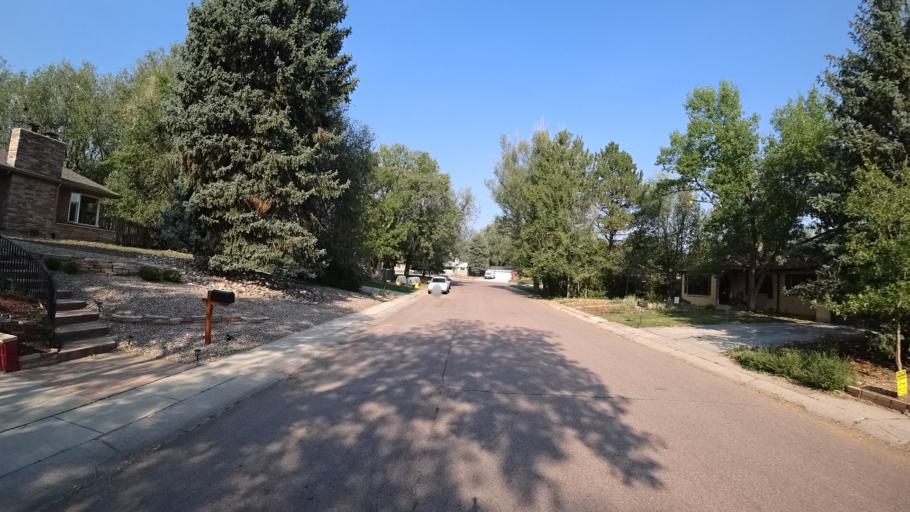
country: US
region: Colorado
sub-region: El Paso County
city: Colorado Springs
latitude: 38.8043
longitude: -104.8466
